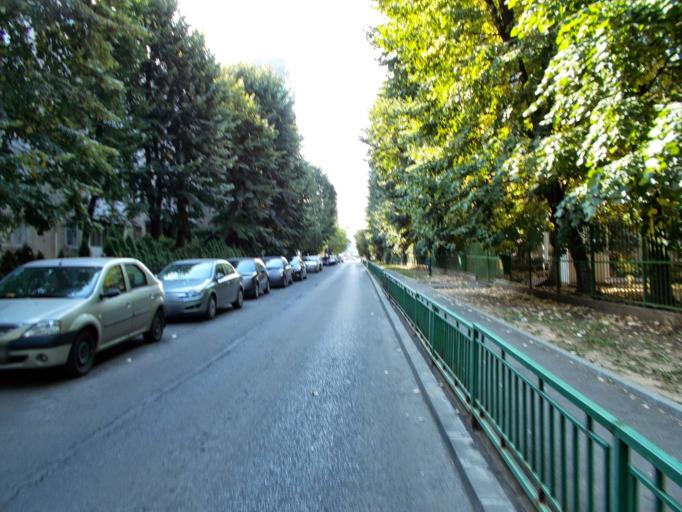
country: RO
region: Ilfov
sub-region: Comuna Popesti-Leordeni
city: Popesti-Leordeni
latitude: 44.3774
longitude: 26.1149
